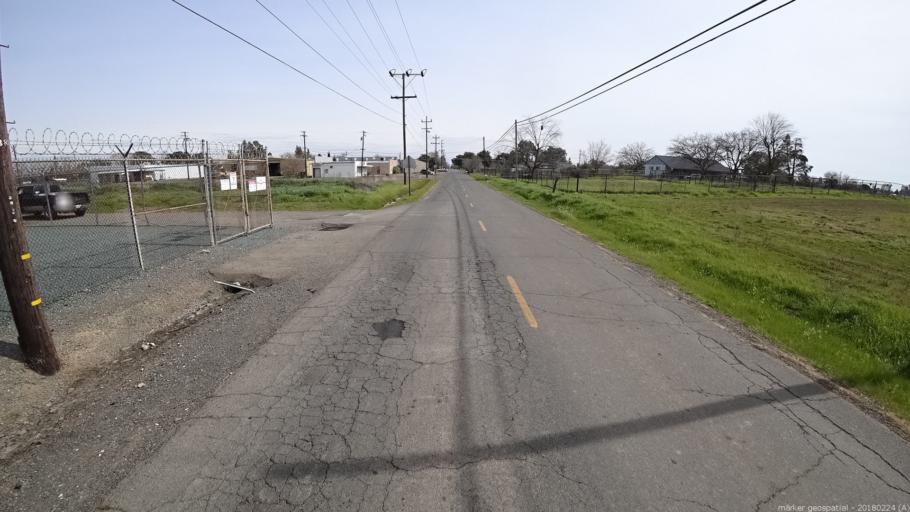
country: US
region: California
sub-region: Sacramento County
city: Elverta
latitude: 38.7100
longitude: -121.4628
